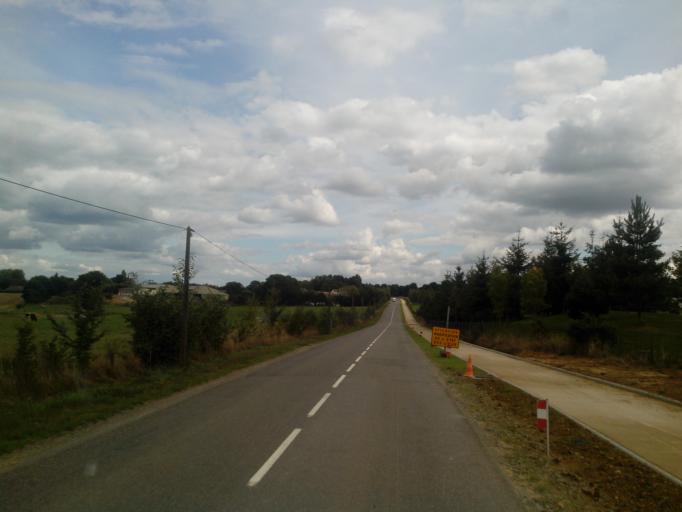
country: FR
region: Brittany
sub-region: Departement d'Ille-et-Vilaine
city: La Chapelle-des-Fougeretz
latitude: 48.2005
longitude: -1.7217
